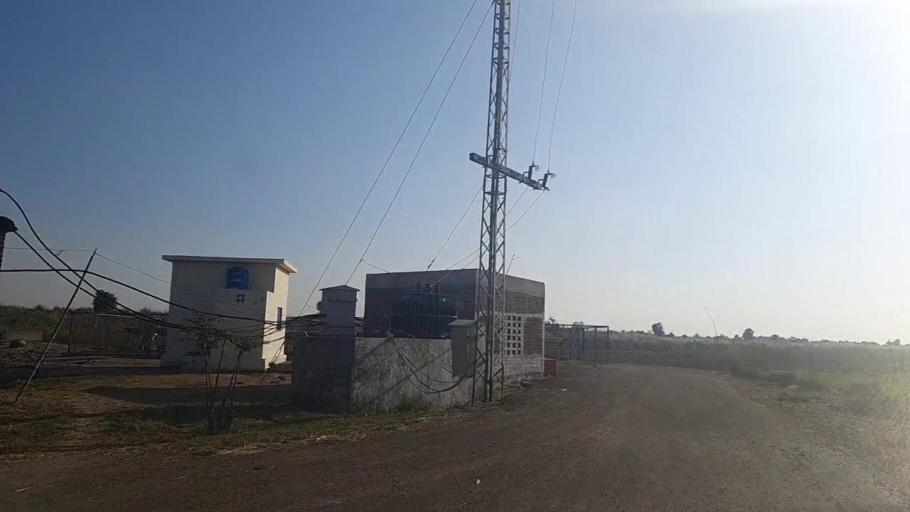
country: PK
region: Sindh
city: Jam Sahib
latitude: 26.3346
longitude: 68.7625
